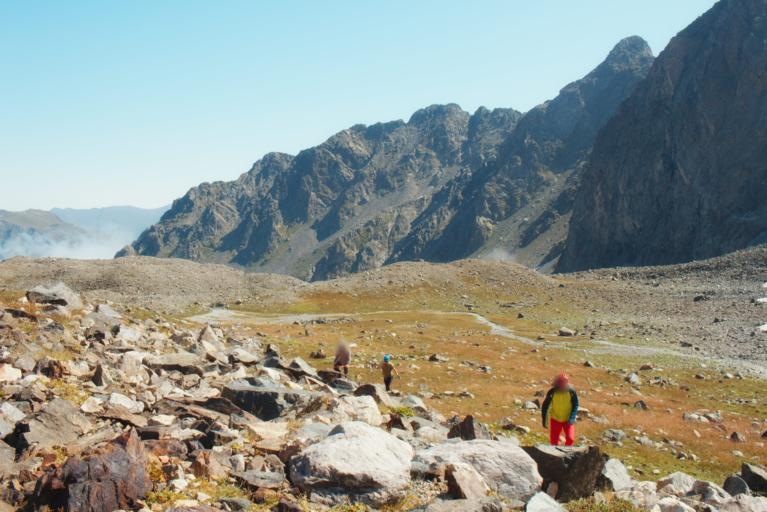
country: RU
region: Karachayevo-Cherkesiya
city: Nizhniy Arkhyz
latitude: 43.4280
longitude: 41.2513
